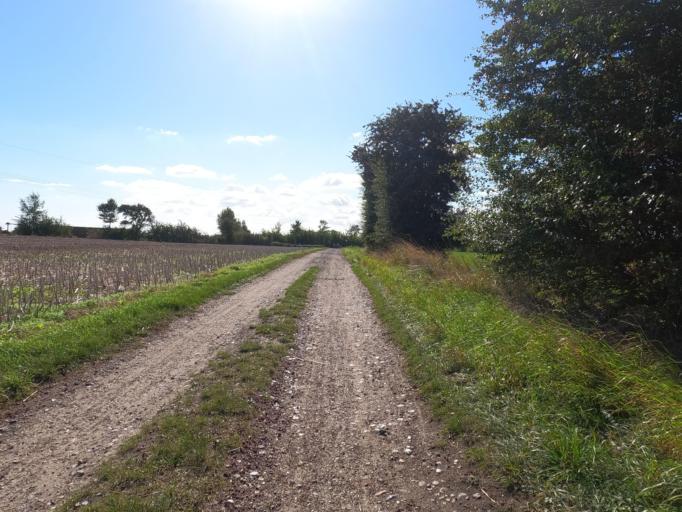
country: DE
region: Schleswig-Holstein
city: Grossenbrode
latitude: 54.3856
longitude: 11.1046
